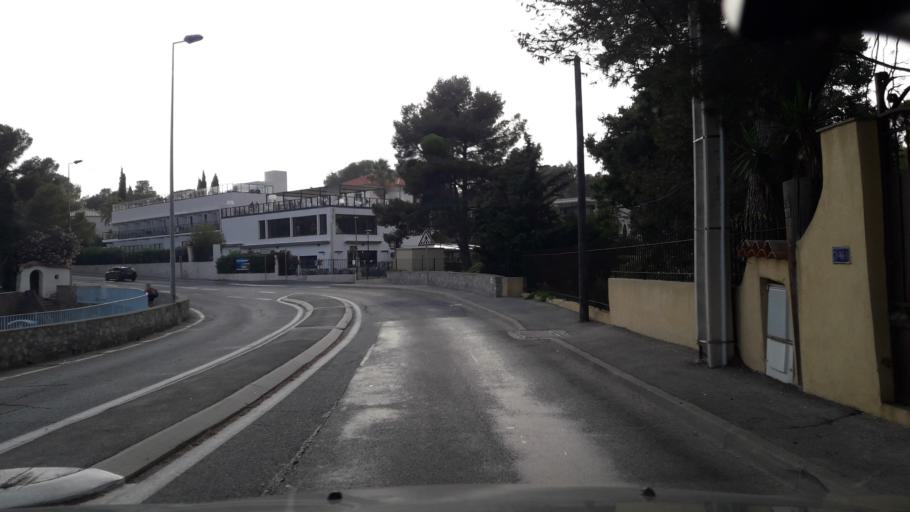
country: FR
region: Provence-Alpes-Cote d'Azur
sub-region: Departement du Var
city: Saint-Raphael
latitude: 43.4179
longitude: 6.8230
